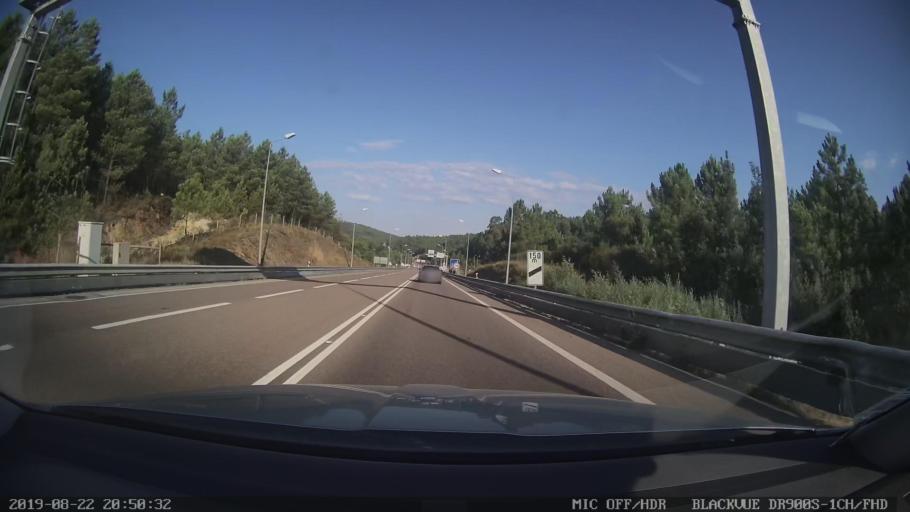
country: PT
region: Castelo Branco
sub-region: Proenca-A-Nova
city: Proenca-a-Nova
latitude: 39.7558
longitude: -7.9410
